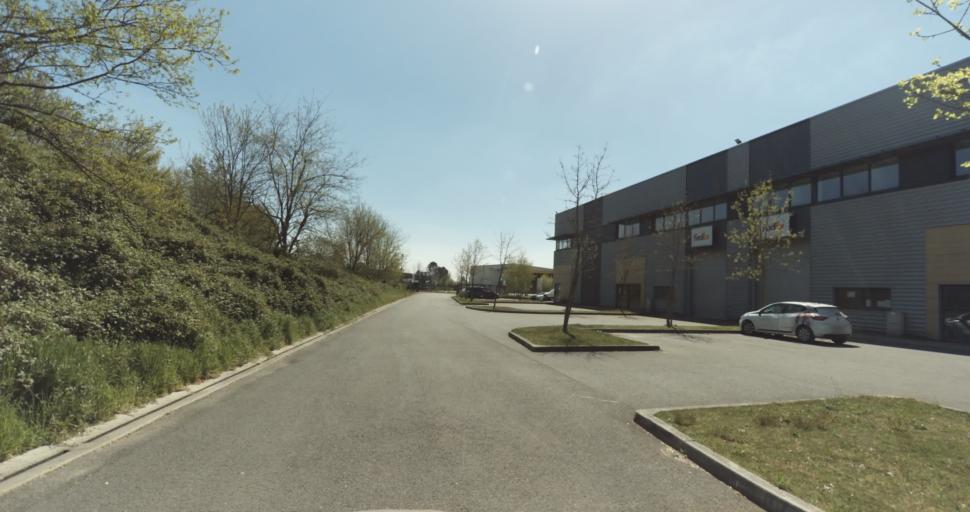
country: FR
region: Aquitaine
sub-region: Departement de la Gironde
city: Martignas-sur-Jalle
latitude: 44.8091
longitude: -0.7457
